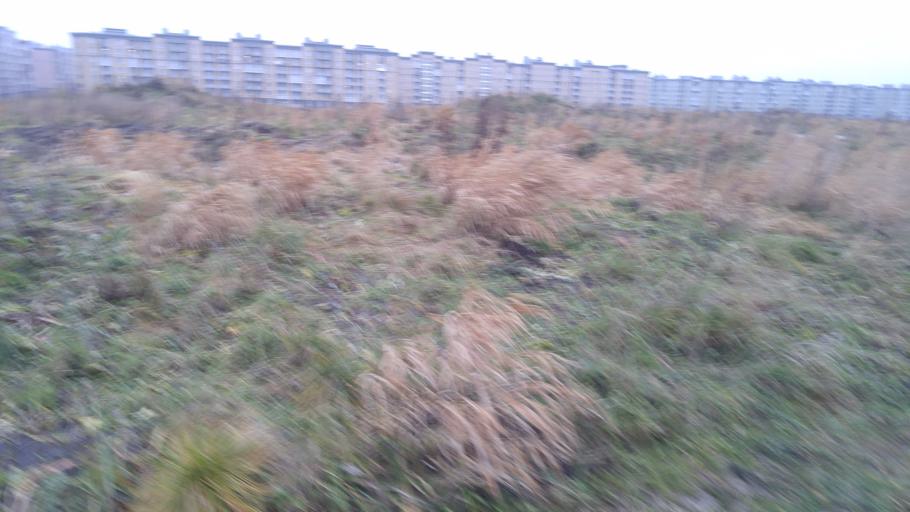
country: RU
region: St.-Petersburg
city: Tyarlevo
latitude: 59.7465
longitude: 30.4874
